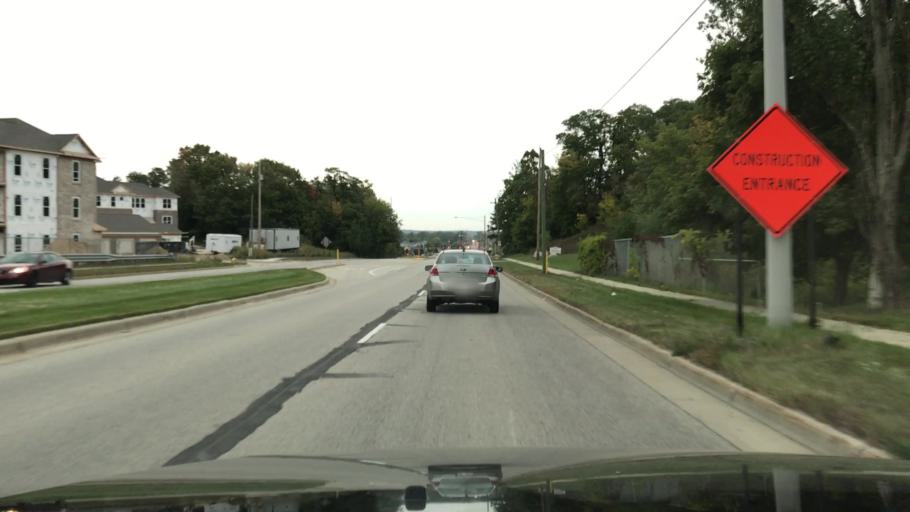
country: US
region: Michigan
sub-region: Kent County
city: Grandville
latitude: 42.8724
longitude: -85.7624
